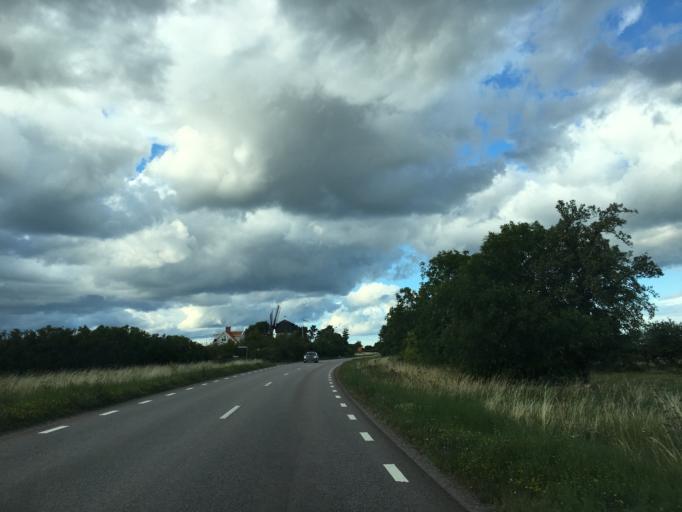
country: SE
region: Kalmar
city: Faerjestaden
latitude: 56.5974
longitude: 16.4698
